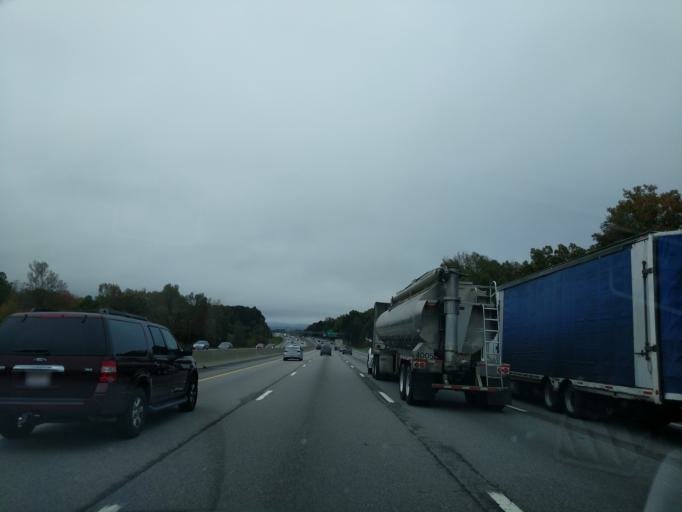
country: US
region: North Carolina
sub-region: Alamance County
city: Mebane
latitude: 36.0747
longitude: -79.1879
